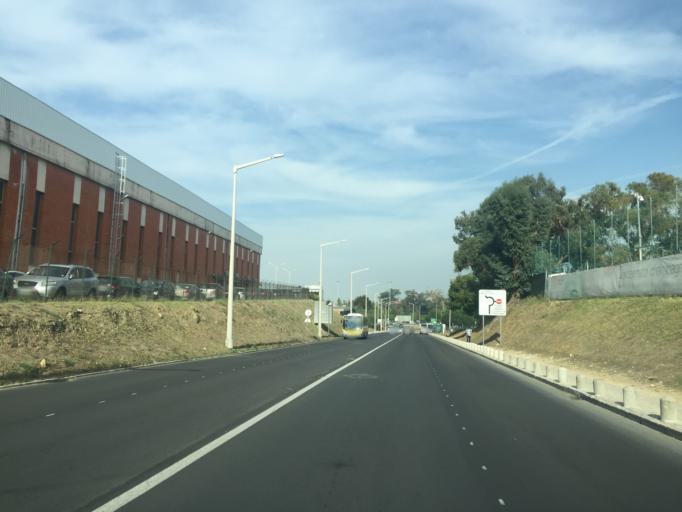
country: PT
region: Lisbon
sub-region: Loures
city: Sacavem
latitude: 38.7786
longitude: -9.1270
